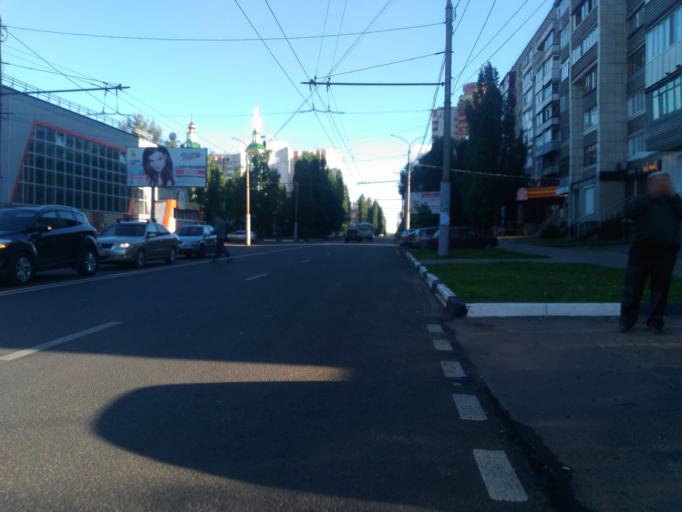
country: RU
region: Voronezj
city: Pridonskoy
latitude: 51.6536
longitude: 39.1213
